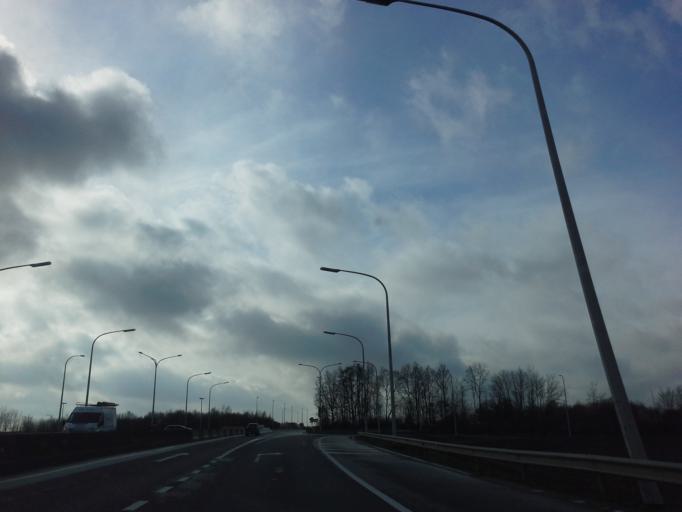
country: BE
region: Flanders
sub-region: Provincie Vlaams-Brabant
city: Tienen
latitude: 50.7831
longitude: 4.9227
